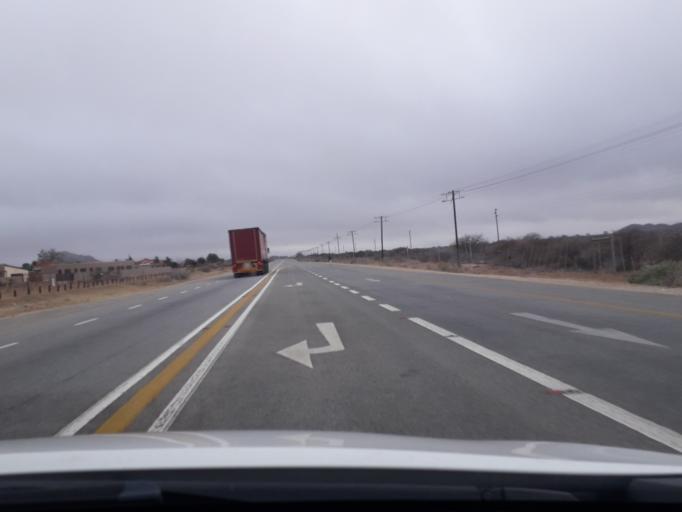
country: ZA
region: Limpopo
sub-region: Capricorn District Municipality
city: Mankoeng
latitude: -23.5199
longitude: 29.7097
